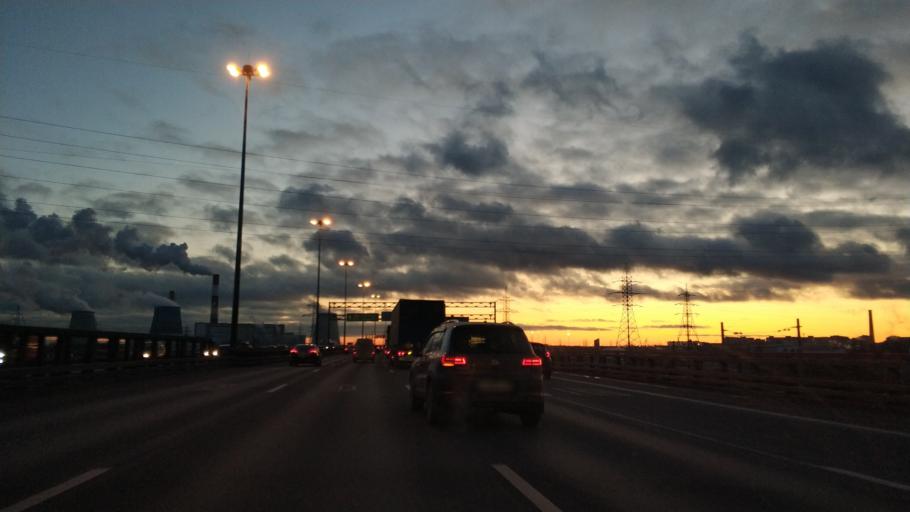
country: RU
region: St.-Petersburg
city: Obukhovo
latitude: 59.8422
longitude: 30.4559
